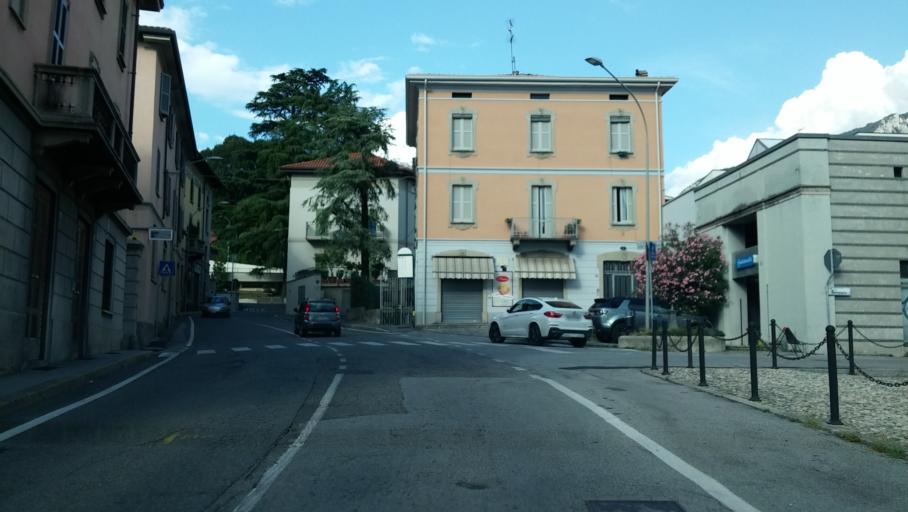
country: IT
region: Lombardy
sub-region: Provincia di Lecco
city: Lecco
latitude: 45.8643
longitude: 9.3940
